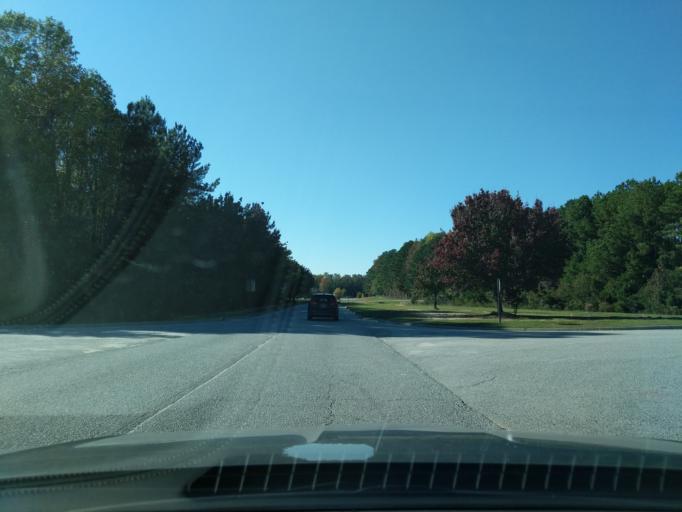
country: US
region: Georgia
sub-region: Columbia County
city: Grovetown
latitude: 33.4664
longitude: -82.1865
